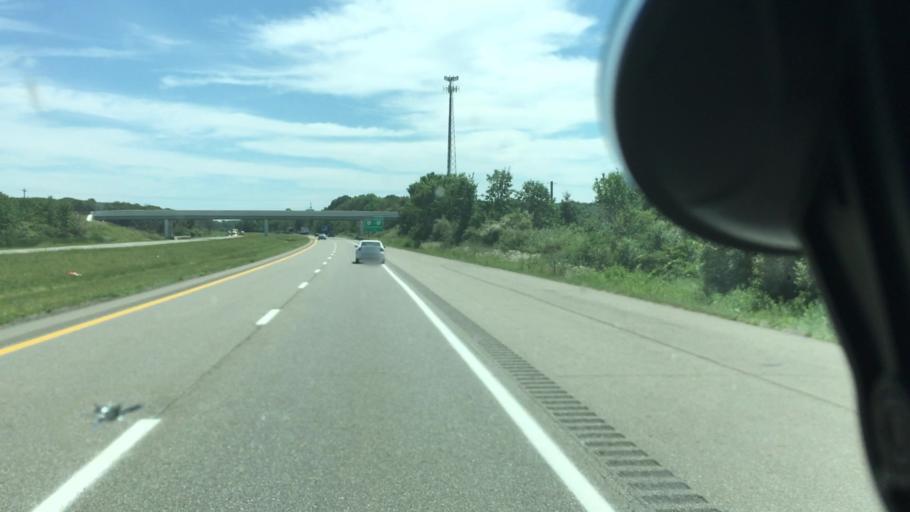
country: US
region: Ohio
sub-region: Columbiana County
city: Columbiana
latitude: 40.9463
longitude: -80.7209
